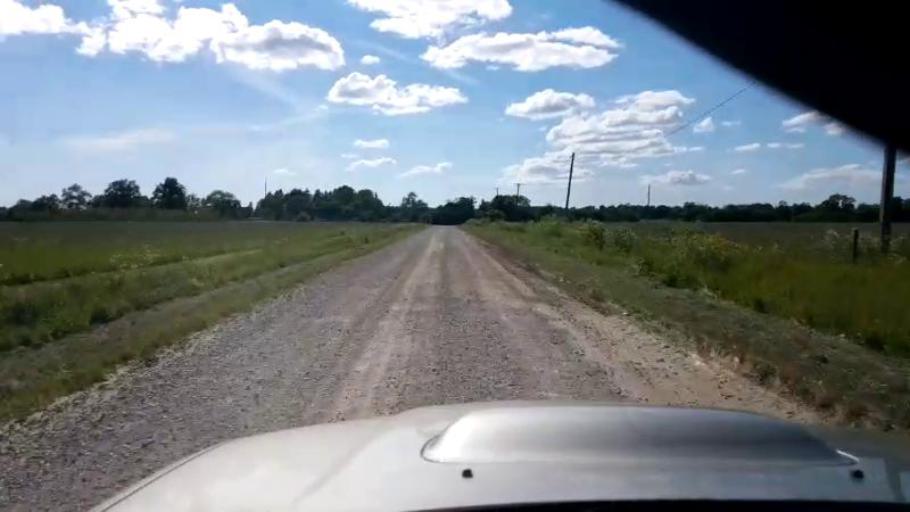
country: EE
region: Paernumaa
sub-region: Sauga vald
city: Sauga
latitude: 58.5088
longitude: 24.5537
